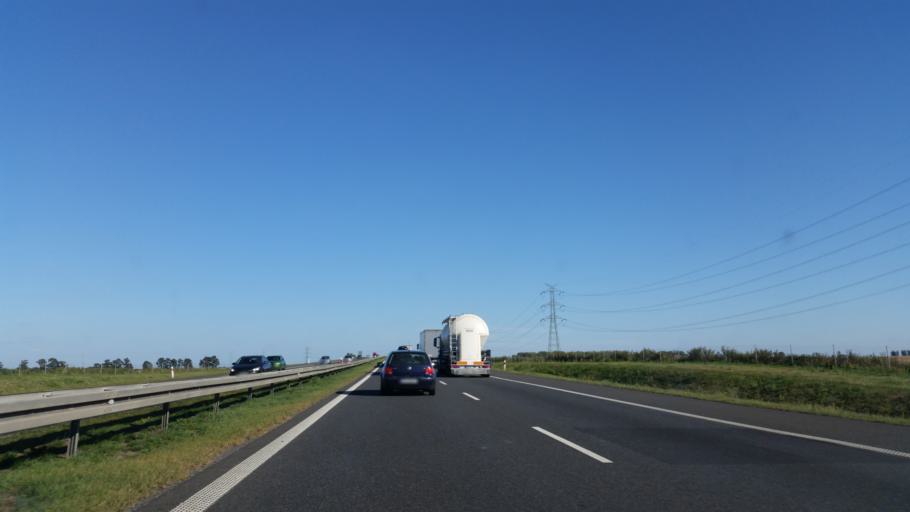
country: PL
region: Opole Voivodeship
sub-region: Powiat brzeski
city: Olszanka
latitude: 50.7524
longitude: 17.4386
